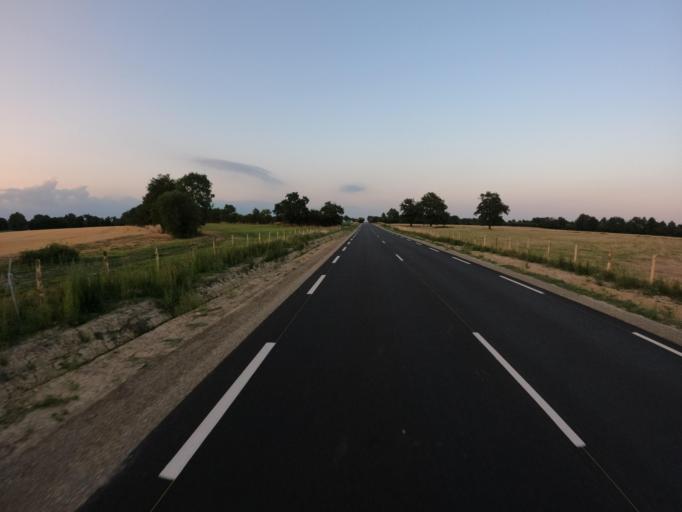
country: FR
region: Pays de la Loire
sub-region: Departement de Maine-et-Loire
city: Segre
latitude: 47.7338
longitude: -0.8399
